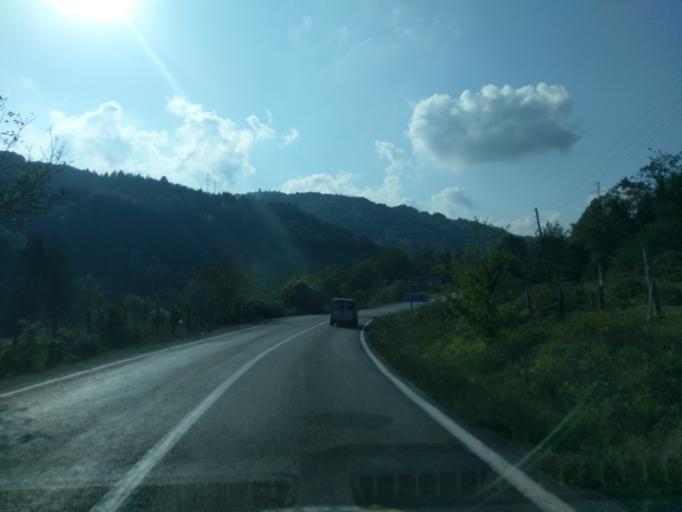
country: TR
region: Sinop
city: Ayancik
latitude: 41.8787
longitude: 34.5298
